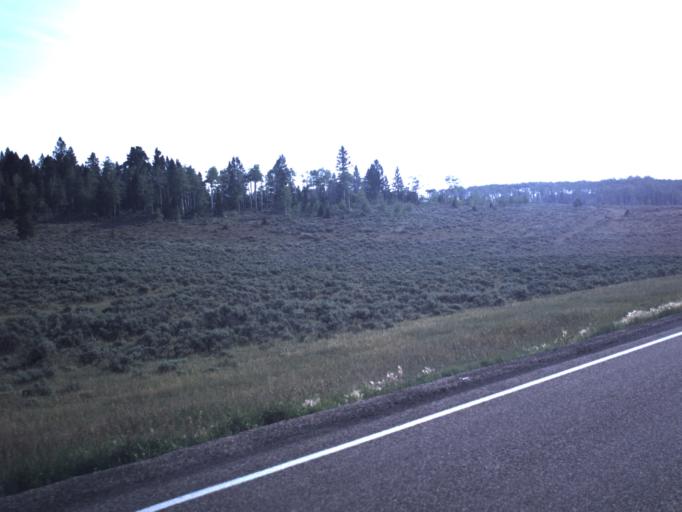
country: US
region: Utah
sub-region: Uintah County
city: Maeser
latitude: 40.7160
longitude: -109.4864
